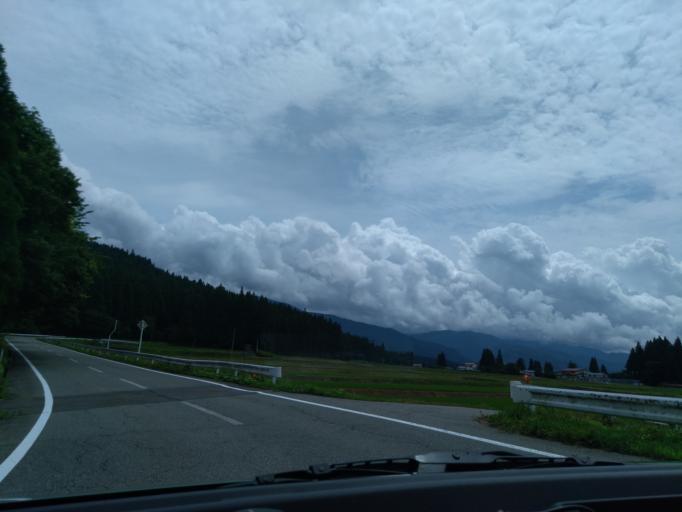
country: JP
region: Akita
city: Kakunodatemachi
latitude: 39.5460
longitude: 140.6341
